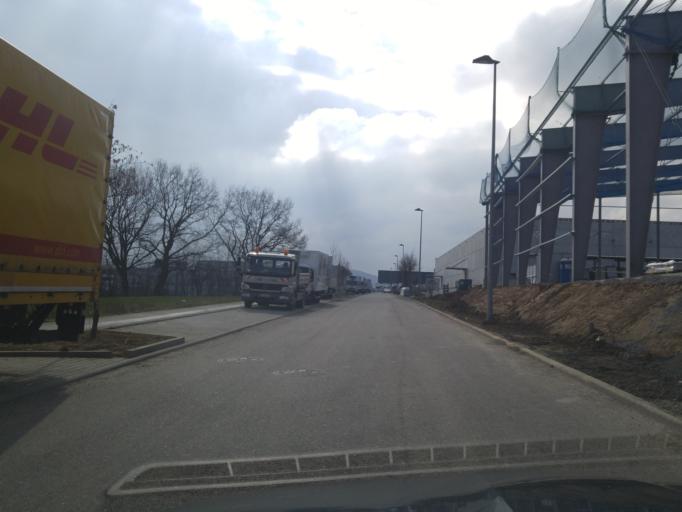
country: DE
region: Baden-Wuerttemberg
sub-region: Regierungsbezirk Stuttgart
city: Ilsfeld
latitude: 49.0676
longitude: 9.2662
